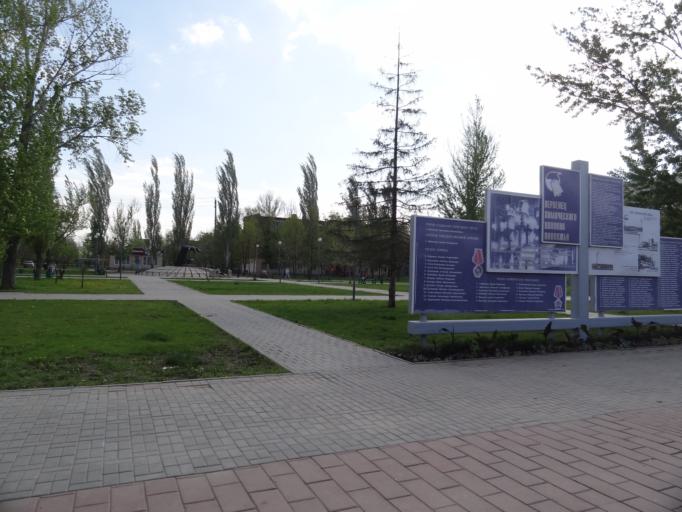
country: RU
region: Saratov
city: Engel's
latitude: 51.4725
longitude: 46.1476
